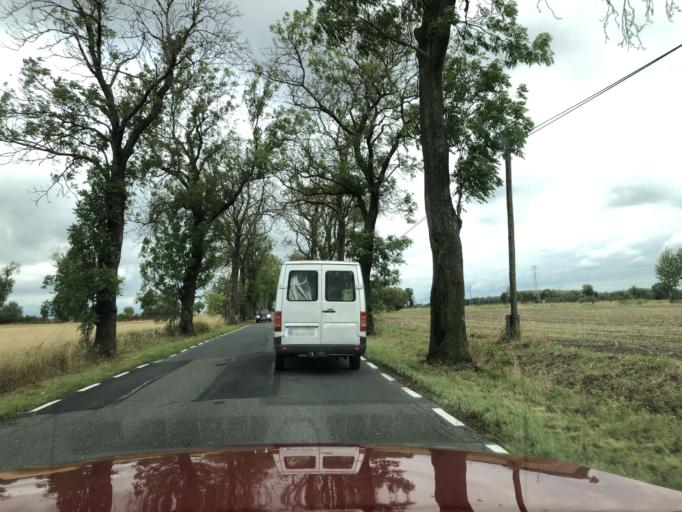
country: PL
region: Greater Poland Voivodeship
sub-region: Powiat miedzychodzki
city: Chrzypsko Wielkie
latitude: 52.5824
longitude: 16.2996
